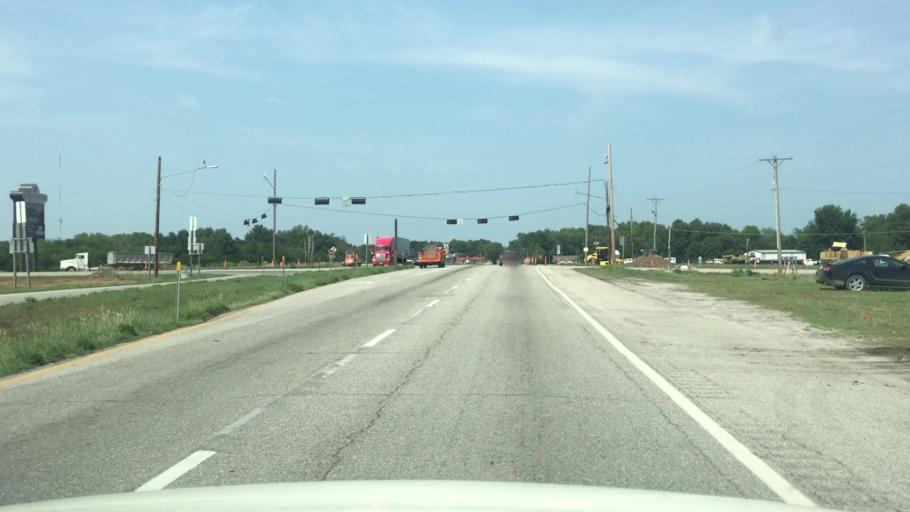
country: US
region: Kansas
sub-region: Crawford County
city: Pittsburg
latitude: 37.3377
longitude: -94.7053
